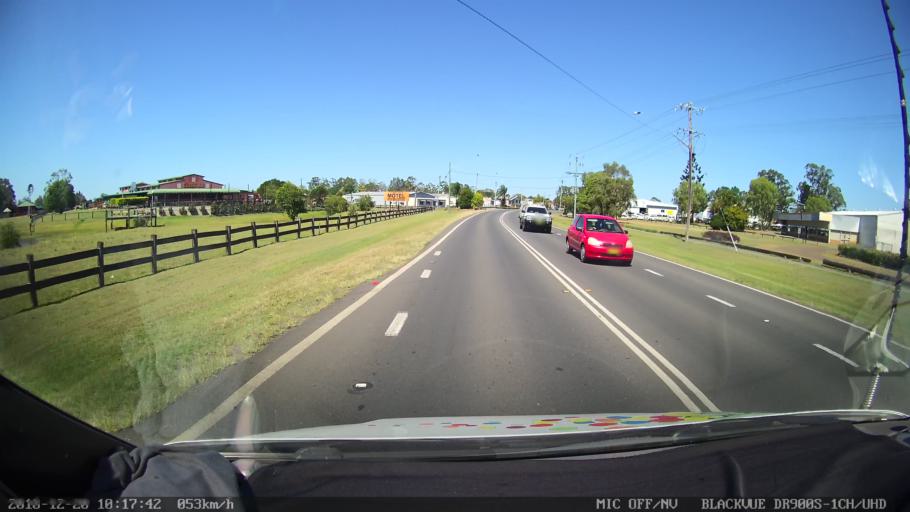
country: AU
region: New South Wales
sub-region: Richmond Valley
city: Casino
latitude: -28.8612
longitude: 153.0683
